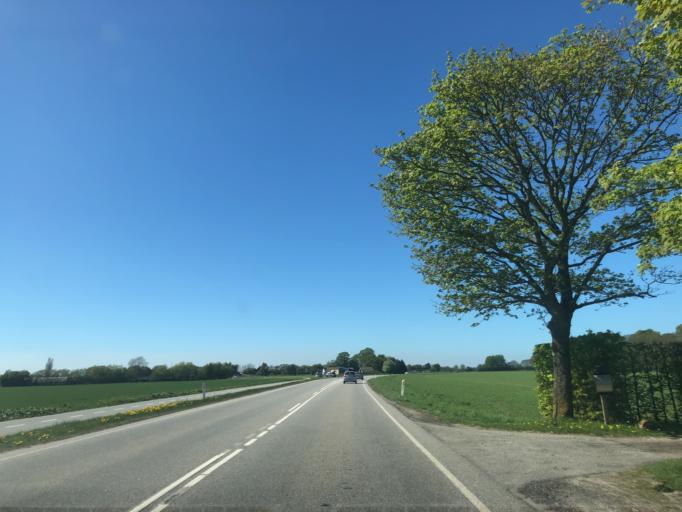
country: DK
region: Zealand
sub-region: Stevns Kommune
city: Store Heddinge
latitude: 55.3392
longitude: 12.3447
